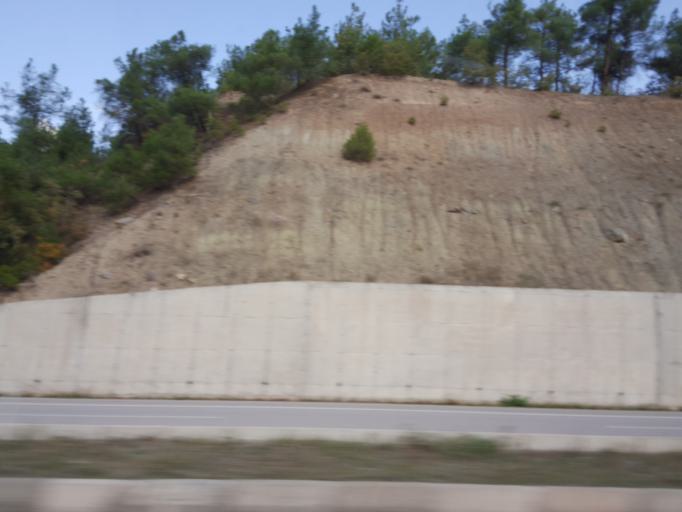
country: TR
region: Tokat
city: Resadiye
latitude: 40.4064
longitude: 37.2405
